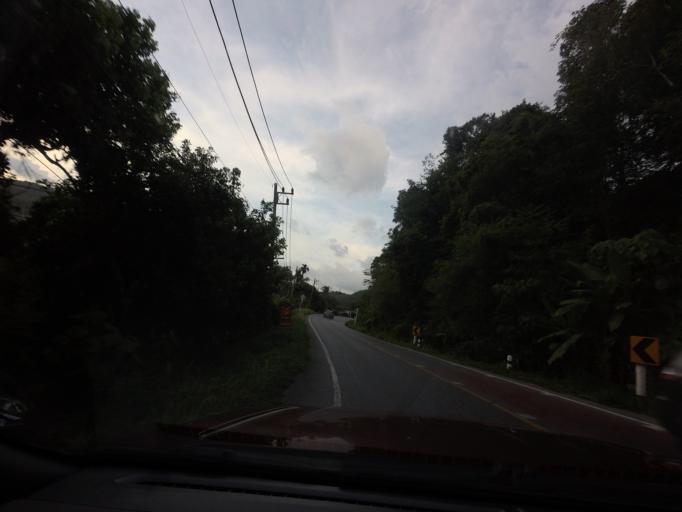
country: TH
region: Yala
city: Than To
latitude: 6.0192
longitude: 101.1998
